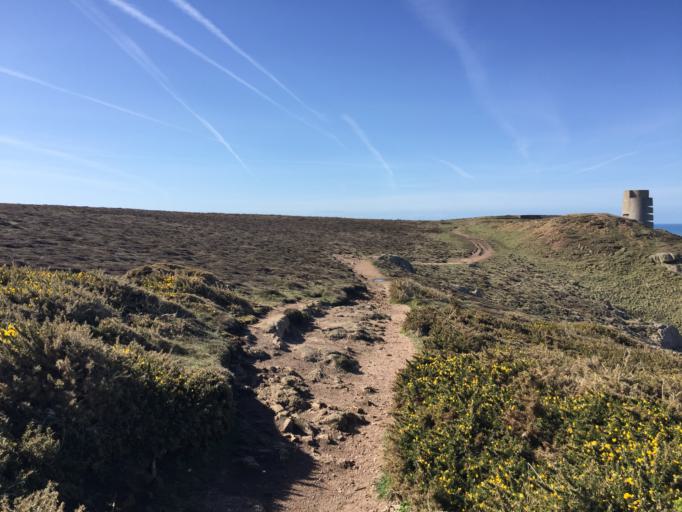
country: JE
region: St Helier
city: Saint Helier
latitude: 49.2533
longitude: -2.2505
